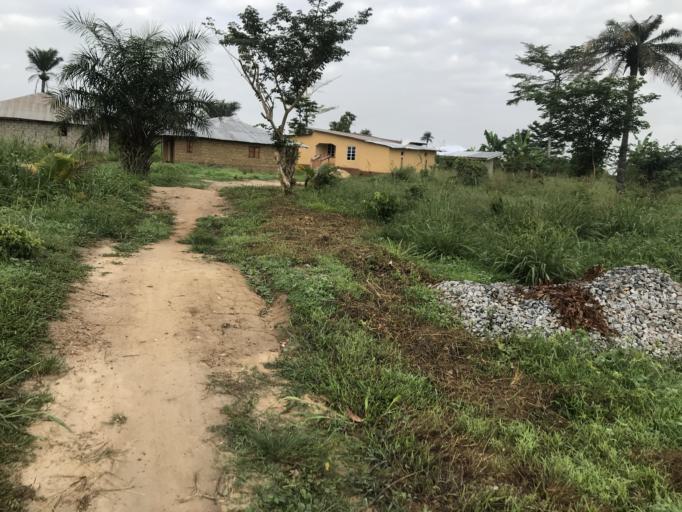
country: SL
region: Eastern Province
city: Pendembu
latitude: 8.0909
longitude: -10.6948
